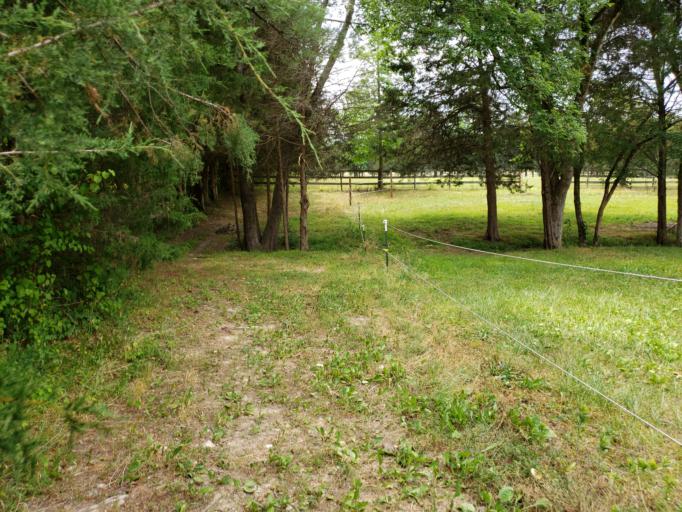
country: US
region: North Carolina
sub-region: Granville County
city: Butner
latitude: 36.1937
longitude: -78.8227
